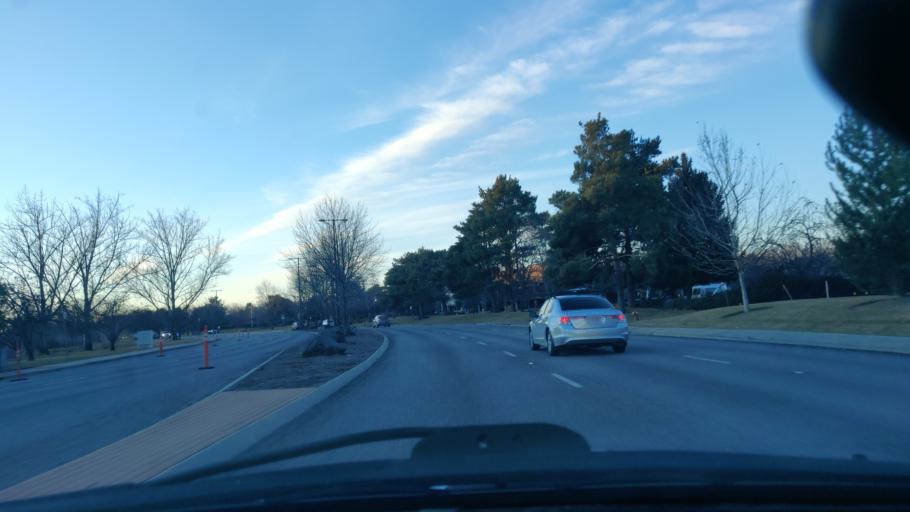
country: US
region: Idaho
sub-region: Ada County
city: Boise
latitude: 43.5977
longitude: -116.1787
